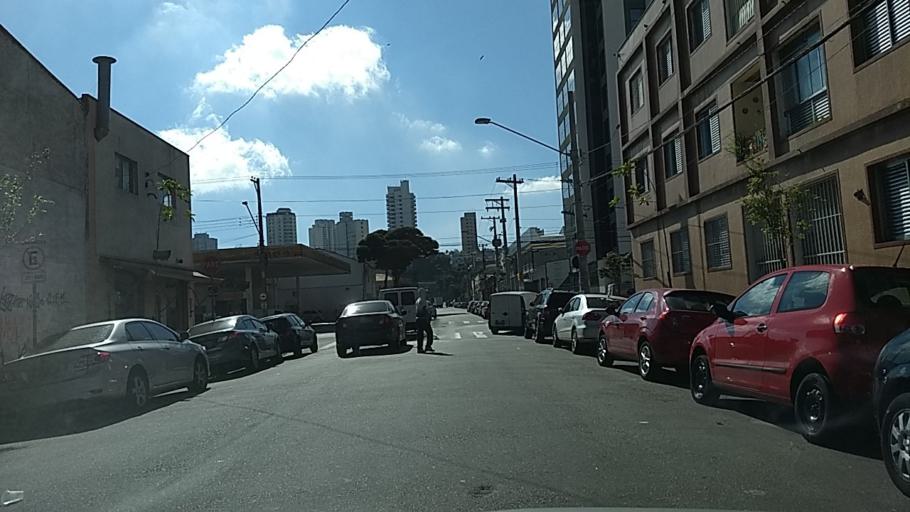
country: BR
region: Sao Paulo
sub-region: Sao Paulo
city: Sao Paulo
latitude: -23.5160
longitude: -46.5864
